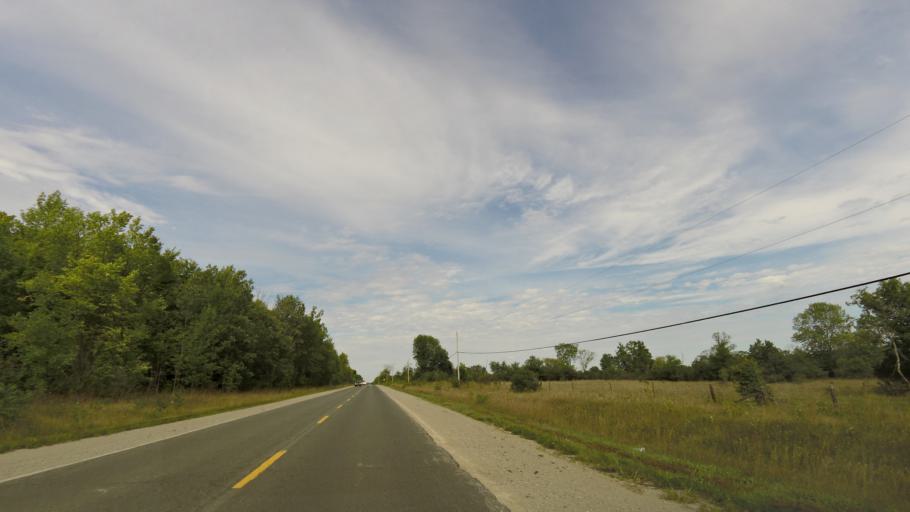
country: CA
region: Ontario
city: Omemee
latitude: 44.6010
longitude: -78.9072
